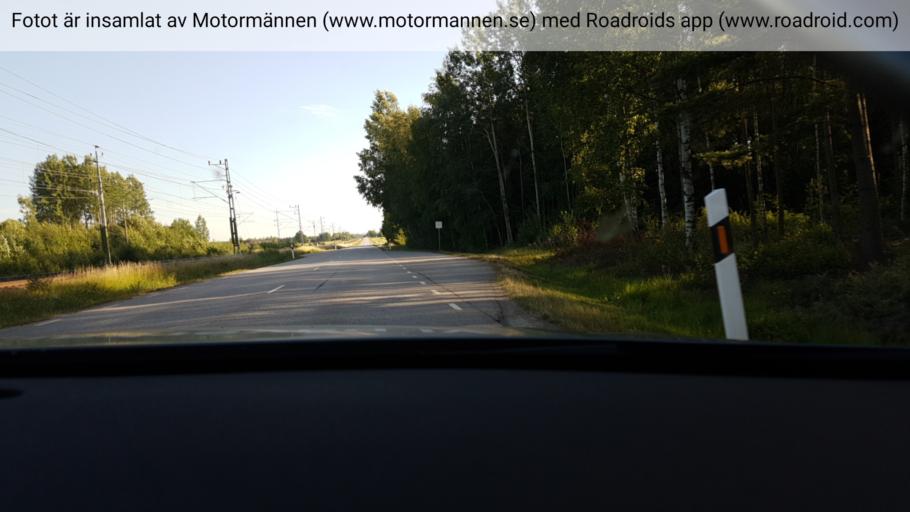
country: SE
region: Vaestra Goetaland
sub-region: Toreboda Kommun
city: Toereboda
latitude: 58.6599
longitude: 14.0867
